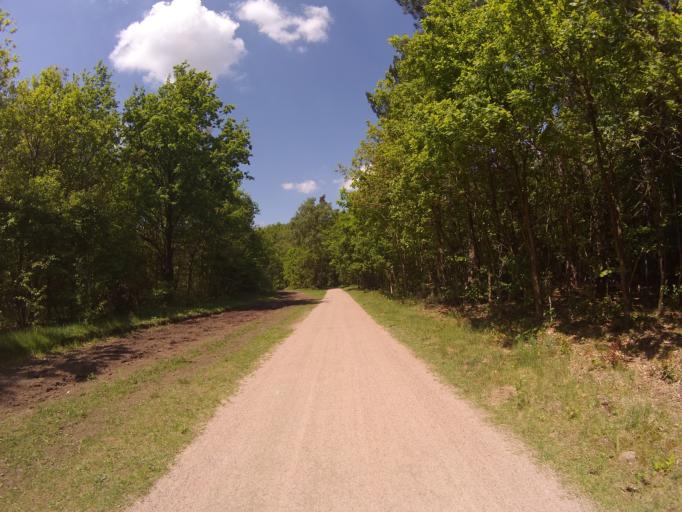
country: NL
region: North Holland
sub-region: Gemeente Laren
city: Laren
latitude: 52.2621
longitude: 5.1985
